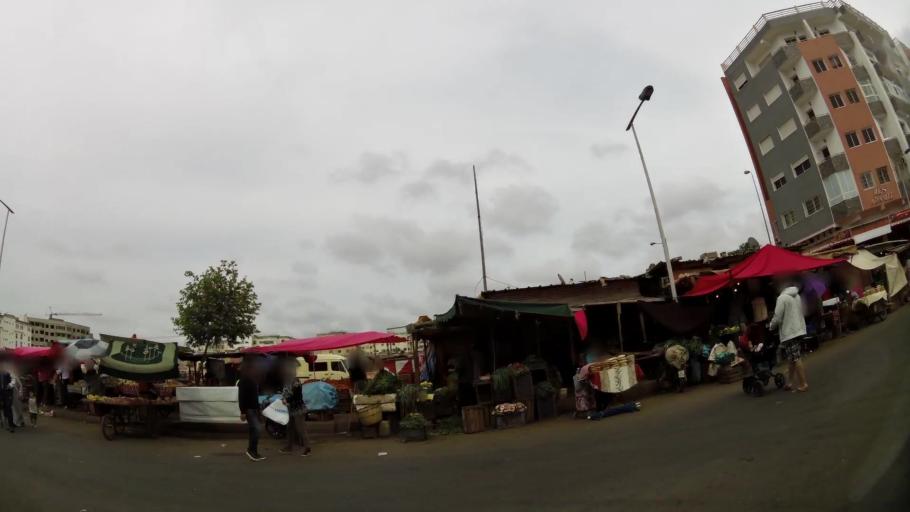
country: MA
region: Rabat-Sale-Zemmour-Zaer
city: Sale
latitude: 34.0432
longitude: -6.8067
